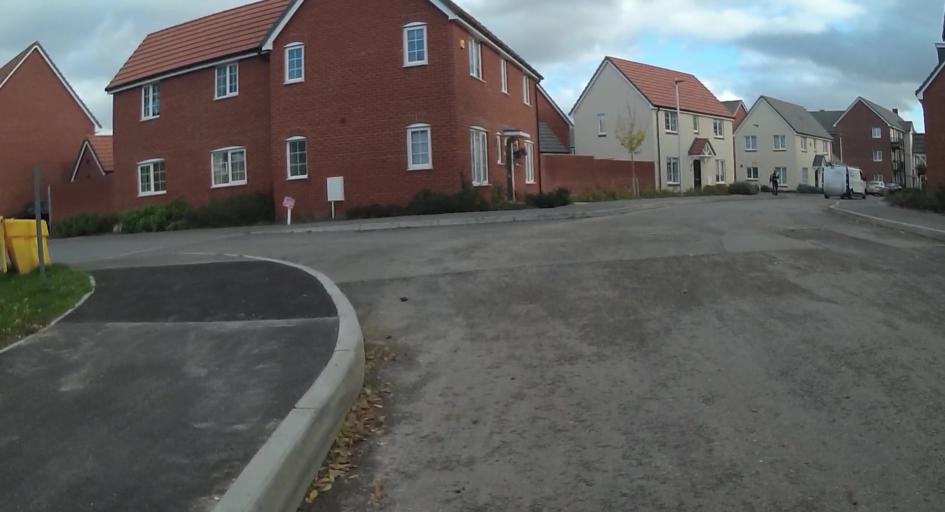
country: GB
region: England
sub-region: Wokingham
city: Shinfield
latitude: 51.3990
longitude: -0.9612
